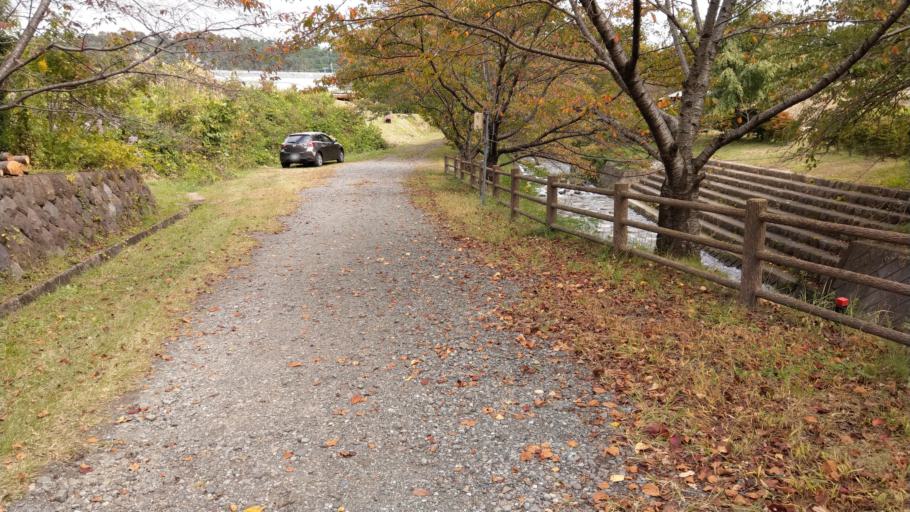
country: JP
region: Nagano
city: Komoro
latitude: 36.3345
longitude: 138.4109
